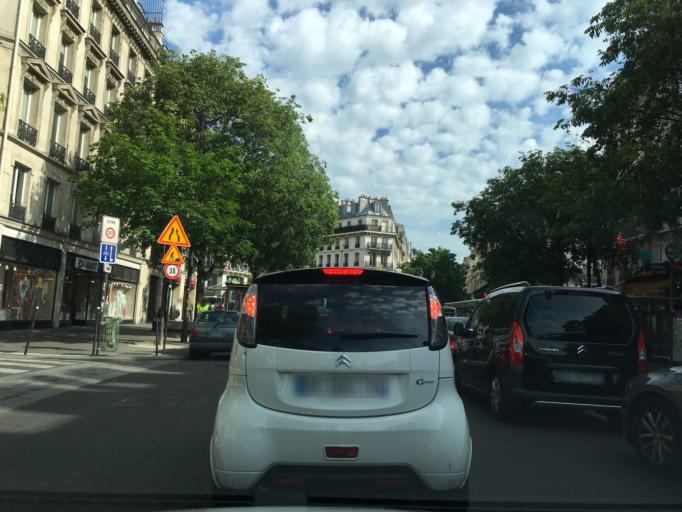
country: FR
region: Ile-de-France
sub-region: Paris
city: Paris
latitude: 48.8582
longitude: 2.3473
